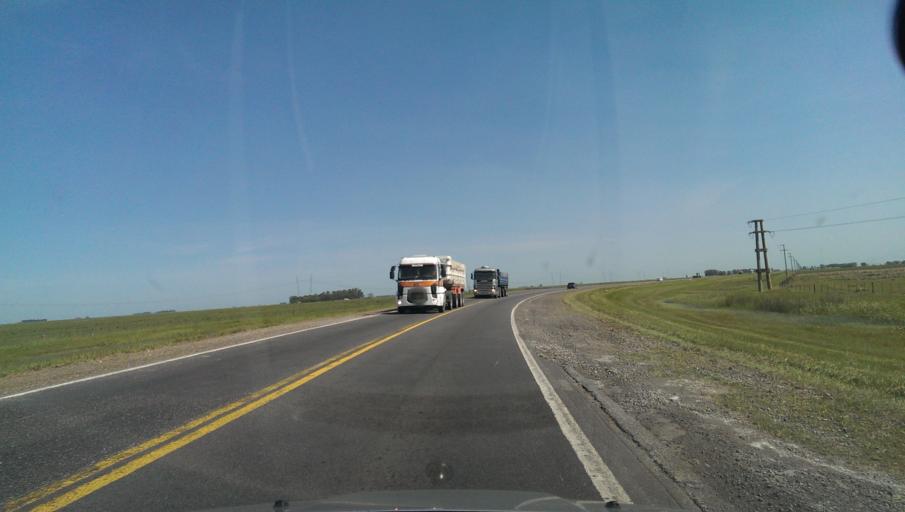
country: AR
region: Buenos Aires
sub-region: Partido de Azul
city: Azul
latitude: -36.5827
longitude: -59.6454
